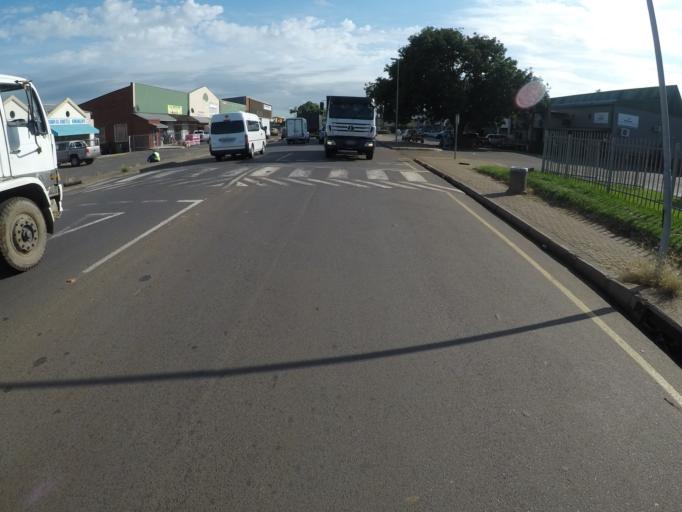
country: ZA
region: KwaZulu-Natal
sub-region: uThungulu District Municipality
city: Empangeni
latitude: -28.7682
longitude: 31.9059
